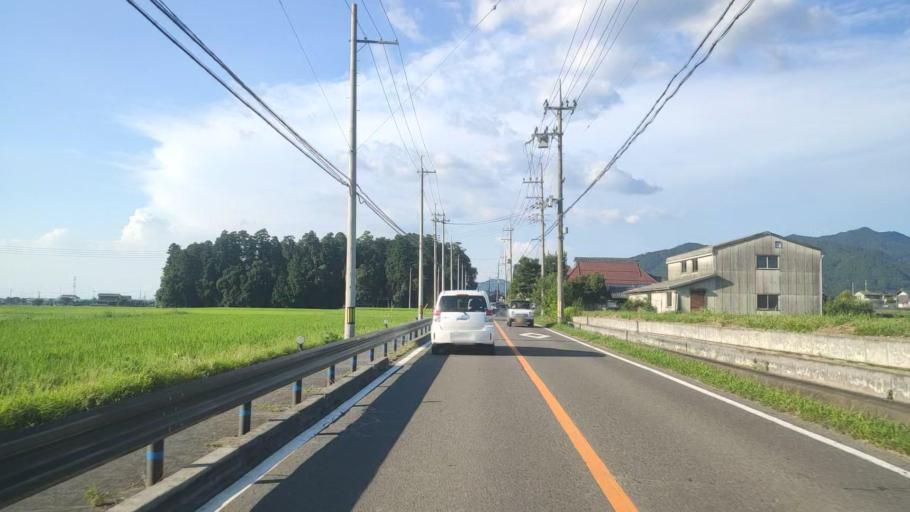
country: JP
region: Shiga Prefecture
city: Youkaichi
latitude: 35.1415
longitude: 136.2632
